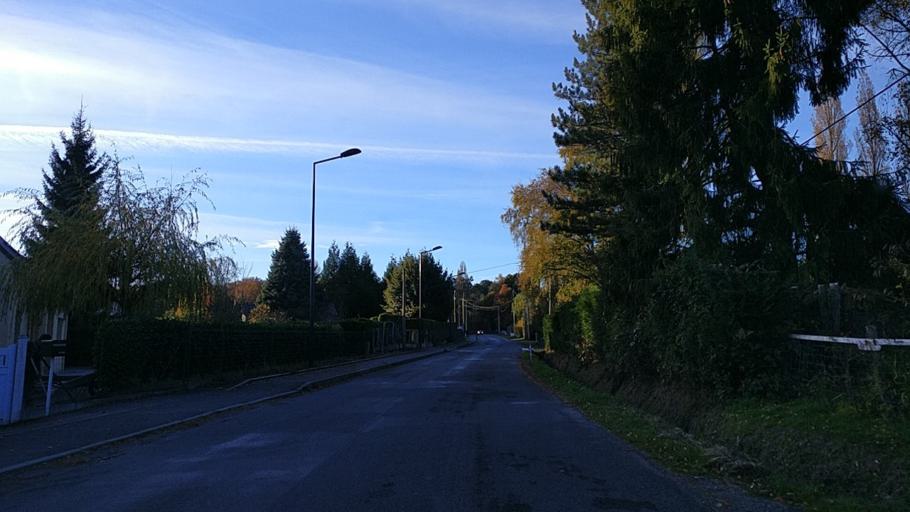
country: FR
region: Brittany
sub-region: Departement d'Ille-et-Vilaine
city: Liffre
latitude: 48.1883
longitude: -1.5204
